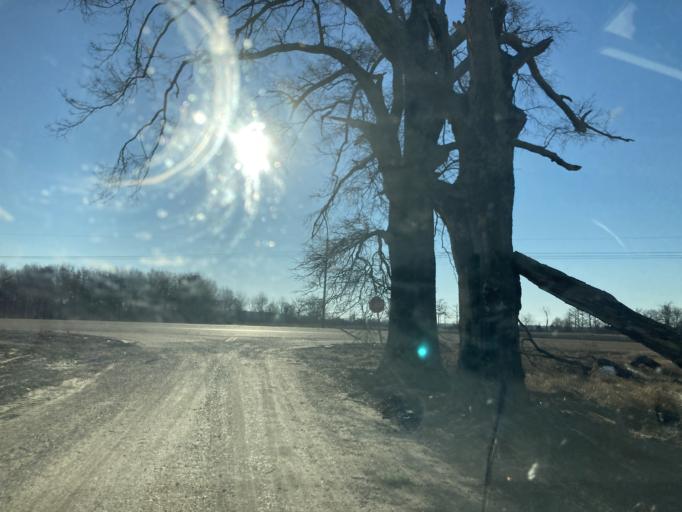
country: US
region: Mississippi
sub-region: Yazoo County
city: Yazoo City
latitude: 32.9220
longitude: -90.6090
